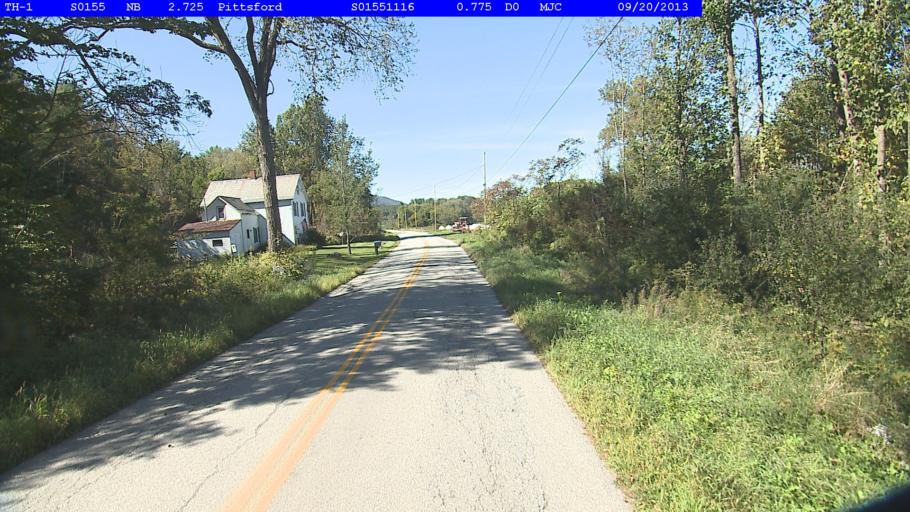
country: US
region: Vermont
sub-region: Rutland County
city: Brandon
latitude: 43.7030
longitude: -73.0455
